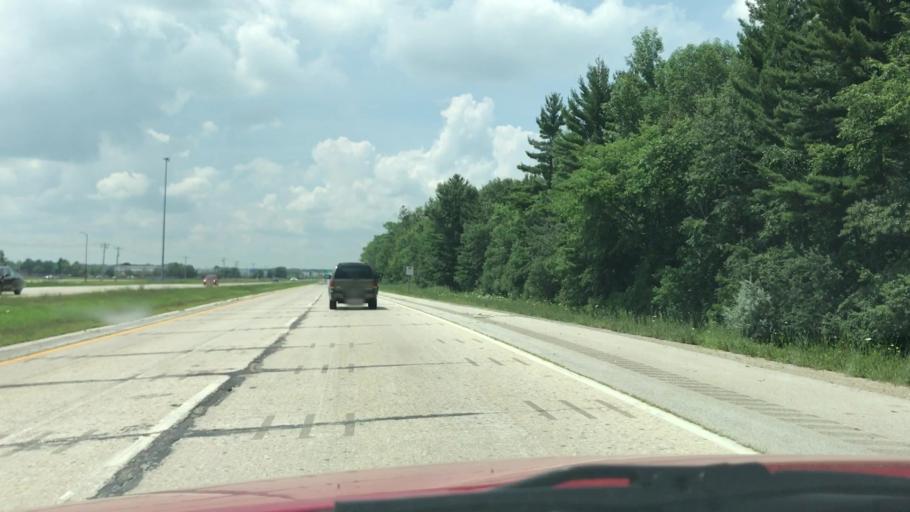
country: US
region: Wisconsin
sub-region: Brown County
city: Ashwaubenon
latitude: 44.4967
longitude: -88.1146
